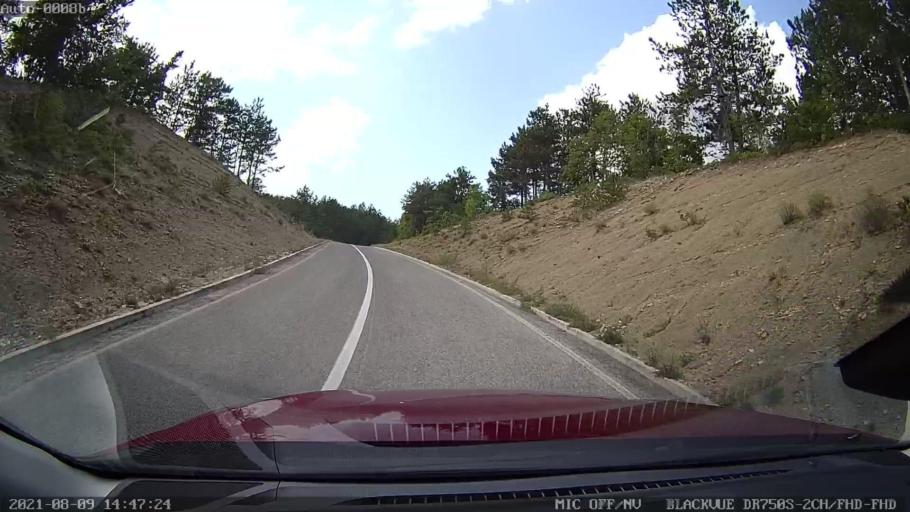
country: HR
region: Istarska
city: Lovran
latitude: 45.2903
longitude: 14.1117
